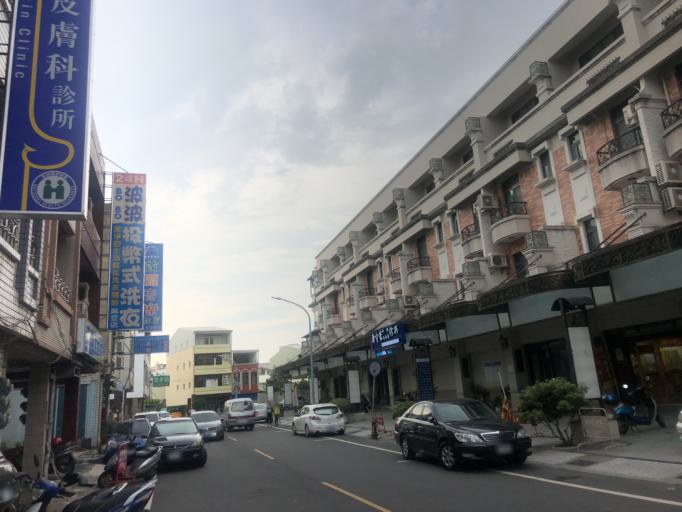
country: TW
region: Taiwan
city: Xinying
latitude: 23.1846
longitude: 120.2452
